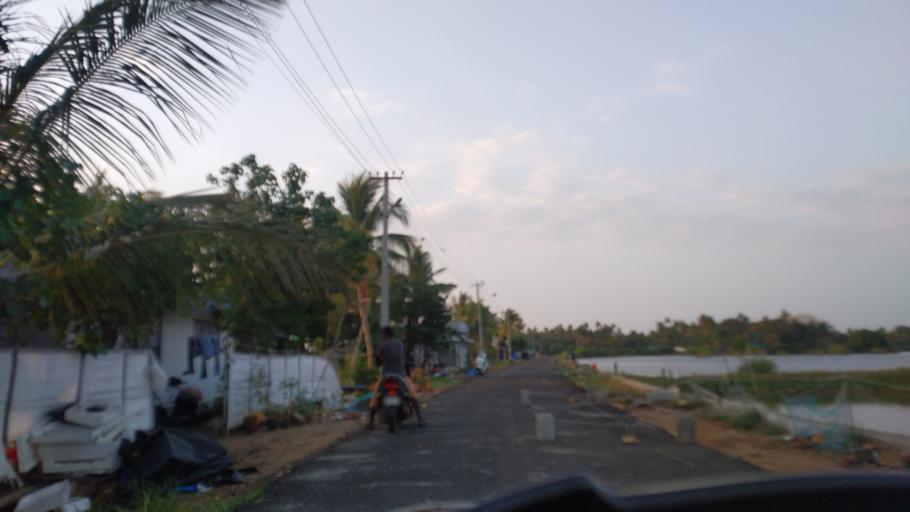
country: IN
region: Kerala
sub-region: Ernakulam
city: Elur
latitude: 10.0517
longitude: 76.2264
